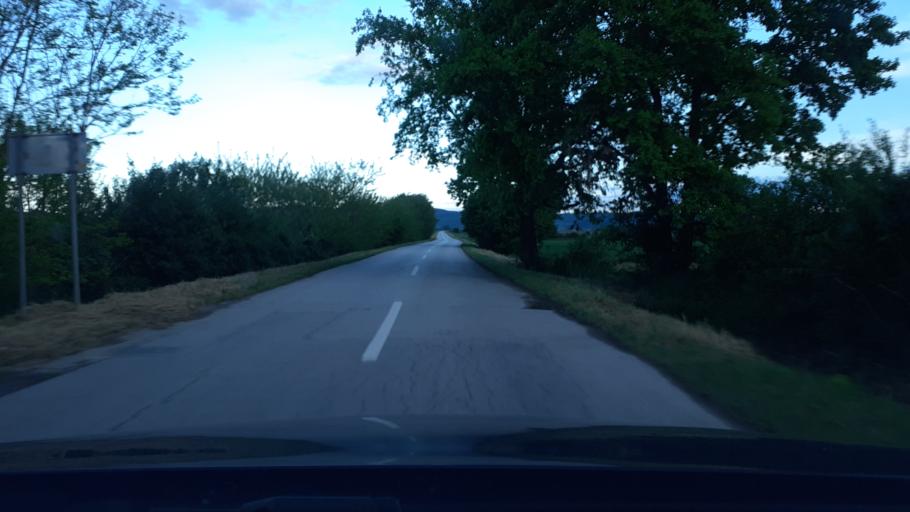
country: HR
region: Pozesko-Slavonska
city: Gradac
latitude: 45.3286
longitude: 17.7999
